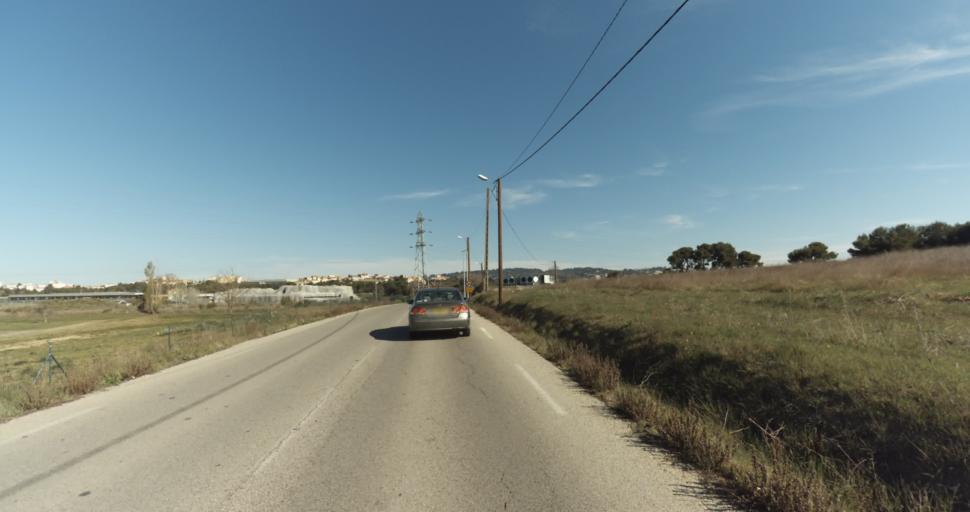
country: FR
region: Provence-Alpes-Cote d'Azur
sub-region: Departement des Bouches-du-Rhone
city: Aix-en-Provence
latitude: 43.5158
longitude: 5.4234
